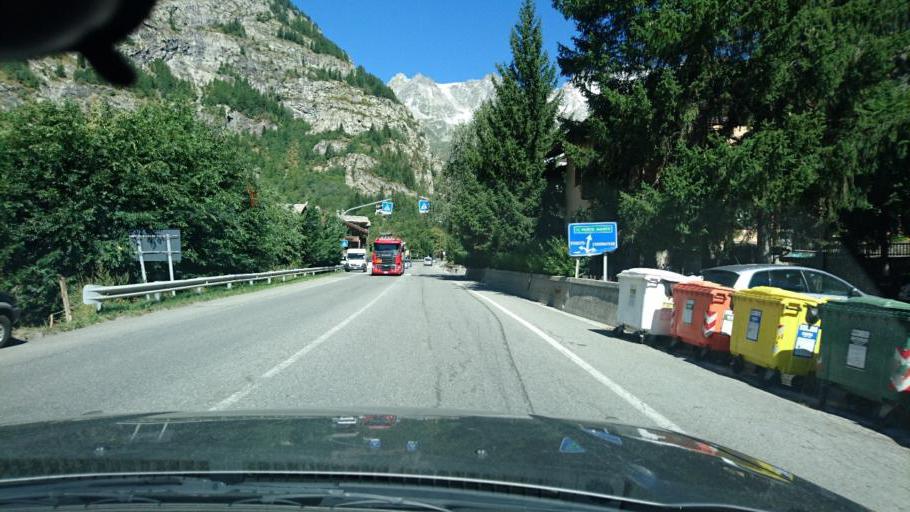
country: IT
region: Aosta Valley
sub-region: Valle d'Aosta
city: Courmayeur
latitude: 45.7930
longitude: 6.9689
